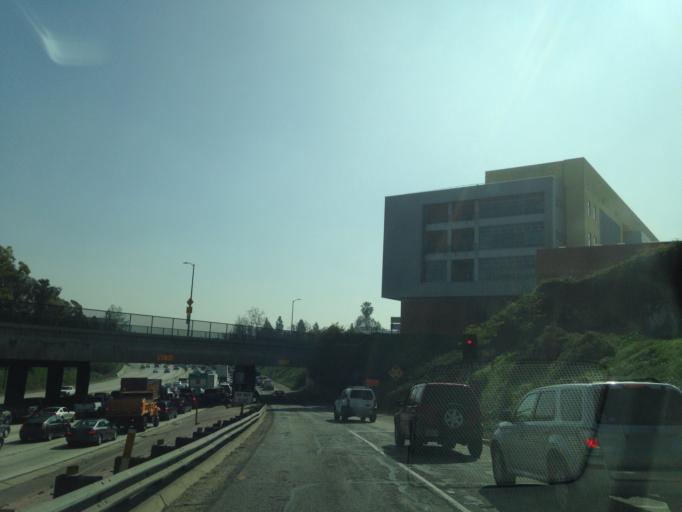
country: US
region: California
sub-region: Los Angeles County
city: Hollywood
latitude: 34.0973
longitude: -118.3143
